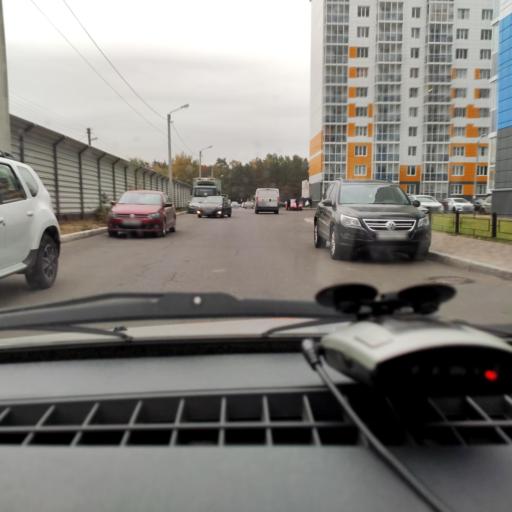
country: RU
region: Voronezj
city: Podgornoye
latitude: 51.7605
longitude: 39.1838
